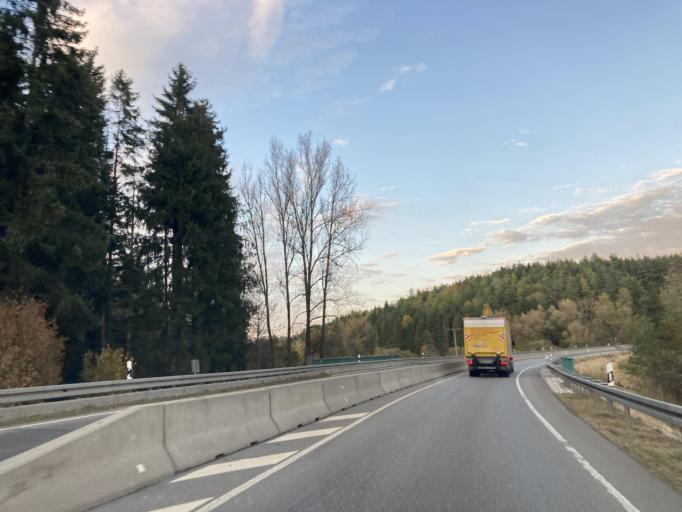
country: DE
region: Baden-Wuerttemberg
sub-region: Tuebingen Region
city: Schomberg
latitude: 48.2190
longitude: 8.7637
